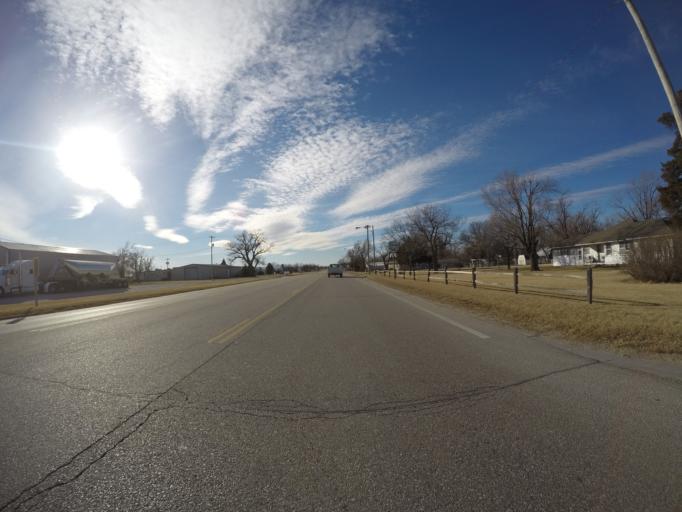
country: US
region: Kansas
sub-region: McPherson County
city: McPherson
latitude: 38.3770
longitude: -97.5390
